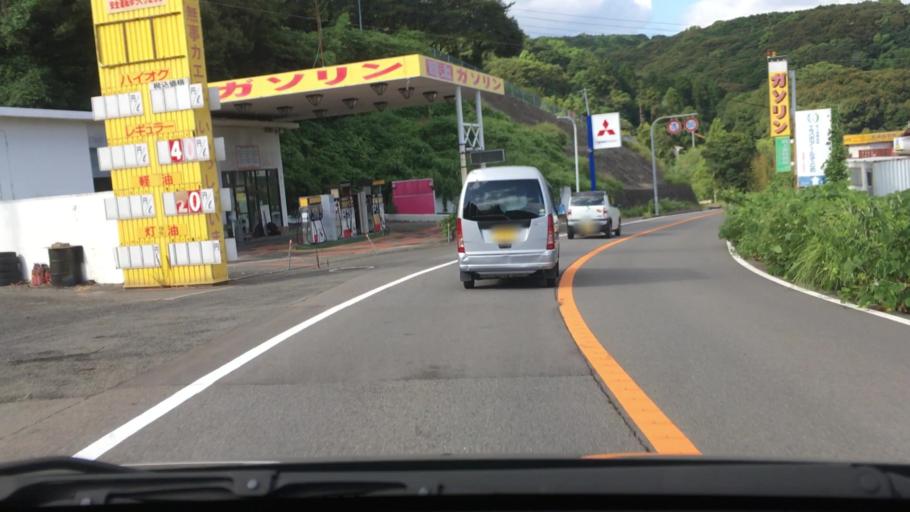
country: JP
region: Nagasaki
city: Togitsu
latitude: 32.8416
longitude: 129.7107
